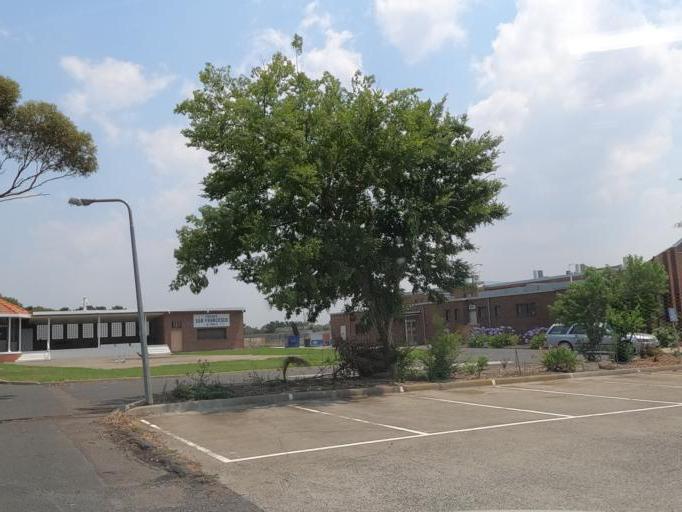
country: AU
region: Victoria
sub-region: Hume
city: Greenvale
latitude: -37.6398
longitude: 144.8245
